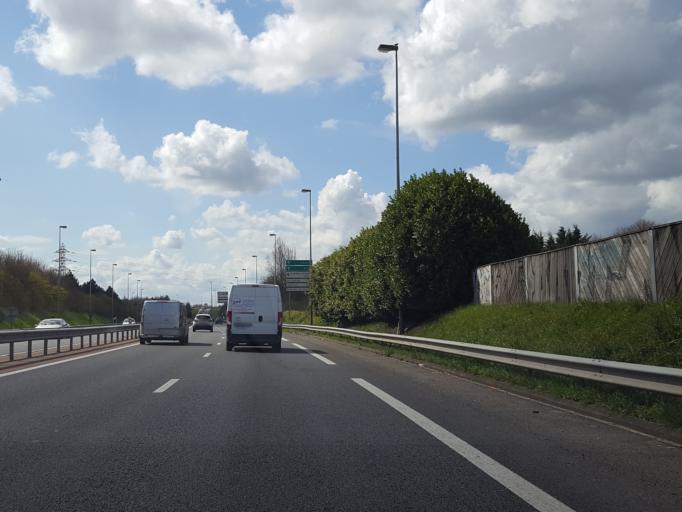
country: FR
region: Centre
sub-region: Departement du Loiret
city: Saran
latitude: 47.9316
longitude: 1.8792
